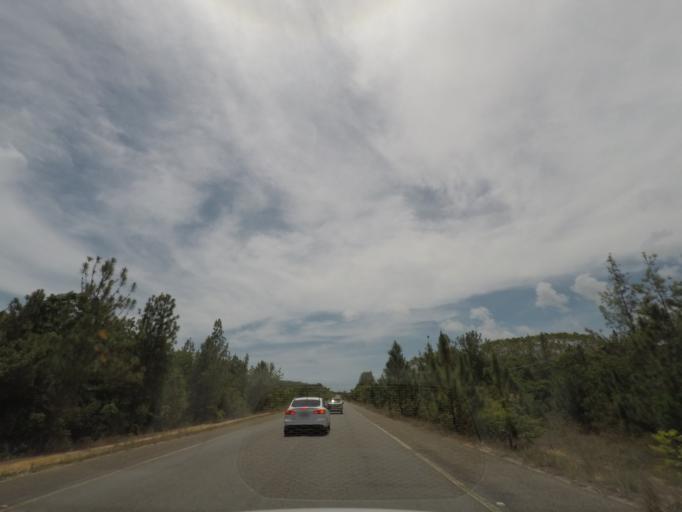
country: BR
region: Bahia
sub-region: Conde
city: Conde
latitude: -12.0142
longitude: -37.6888
